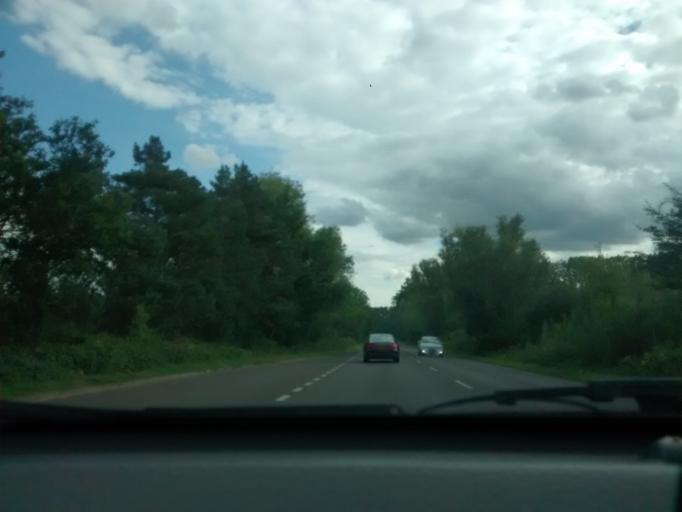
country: GB
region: England
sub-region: Norfolk
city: Downham Market
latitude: 52.5749
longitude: 0.3894
